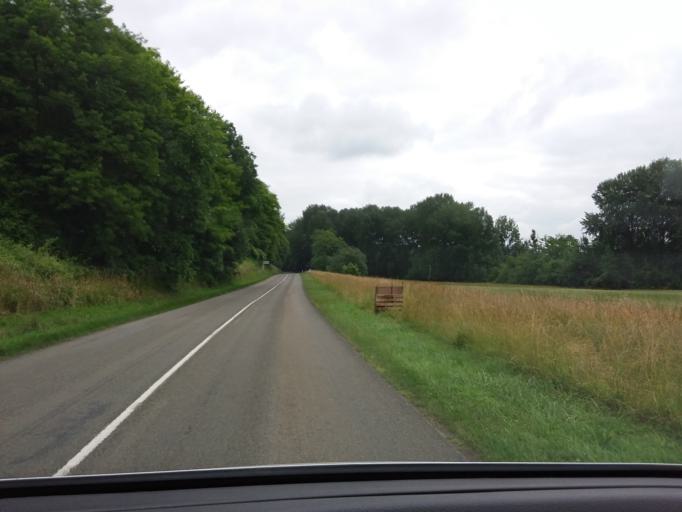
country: FR
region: Picardie
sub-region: Departement de l'Aisne
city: Vailly-sur-Aisne
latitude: 49.4060
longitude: 3.4880
